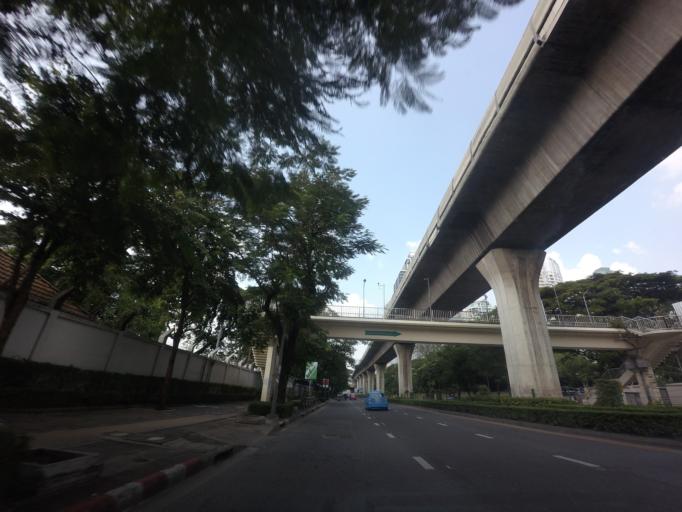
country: TH
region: Bangkok
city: Pathum Wan
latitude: 13.7367
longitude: 100.5390
